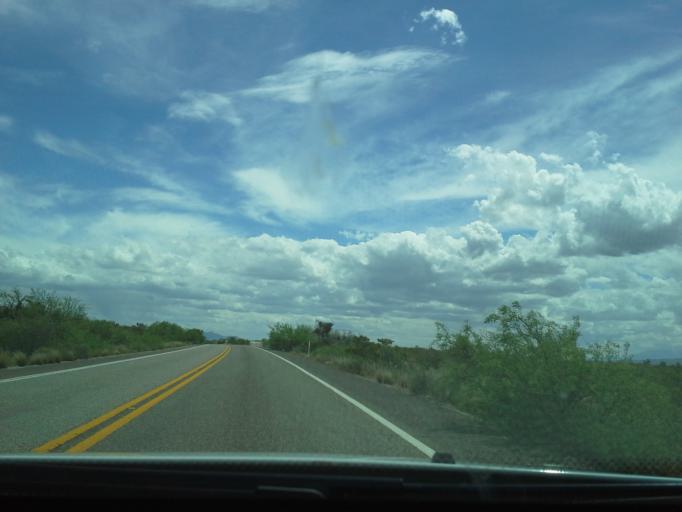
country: US
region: Arizona
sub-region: Gila County
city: Peridot
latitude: 33.2577
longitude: -110.2924
